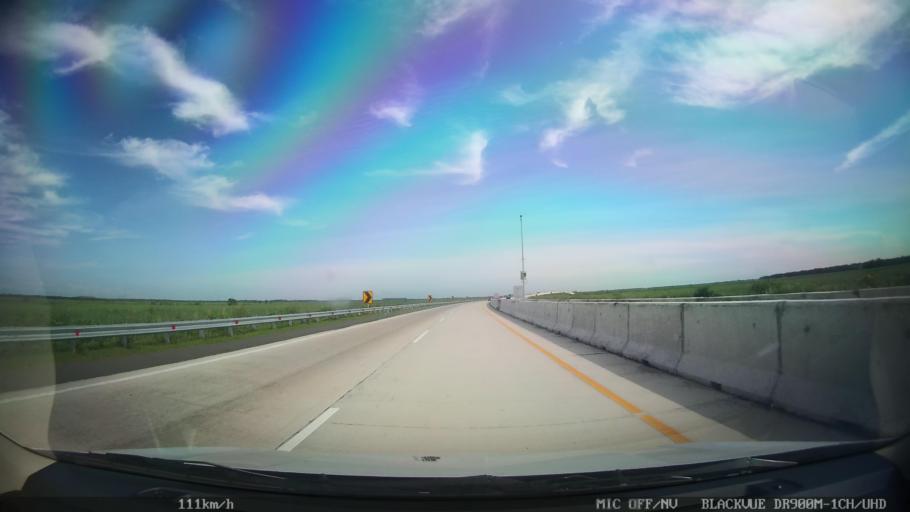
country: ID
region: North Sumatra
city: Binjai
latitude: 3.6573
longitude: 98.5333
